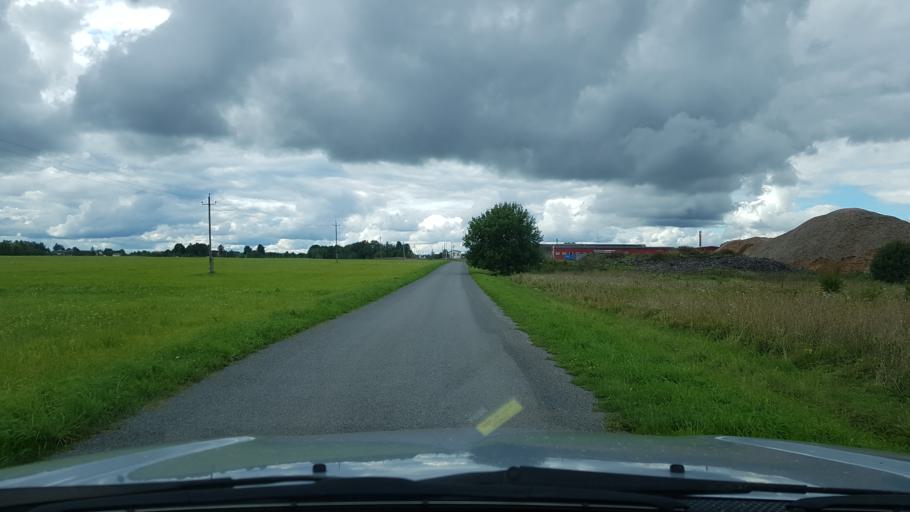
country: EE
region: Harju
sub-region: Rae vald
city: Vaida
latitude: 59.2940
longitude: 24.9846
